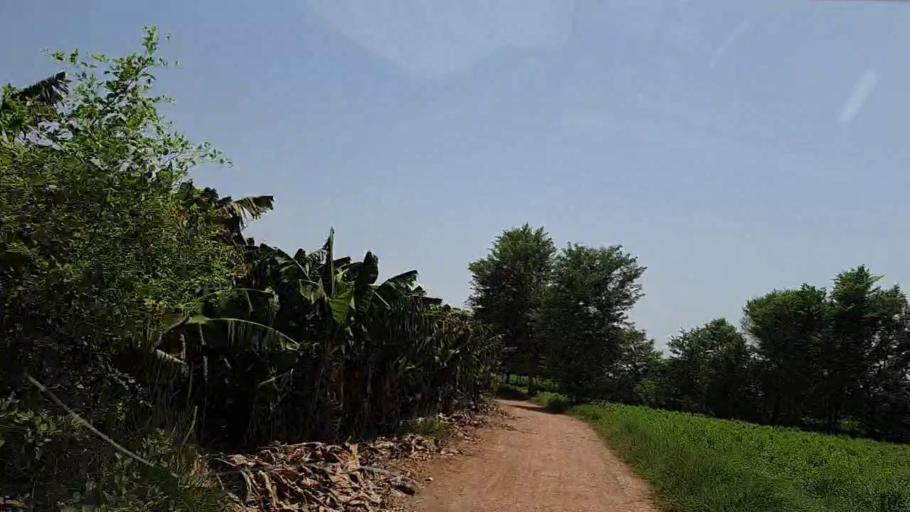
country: PK
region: Sindh
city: Tharu Shah
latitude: 26.9337
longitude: 68.0380
